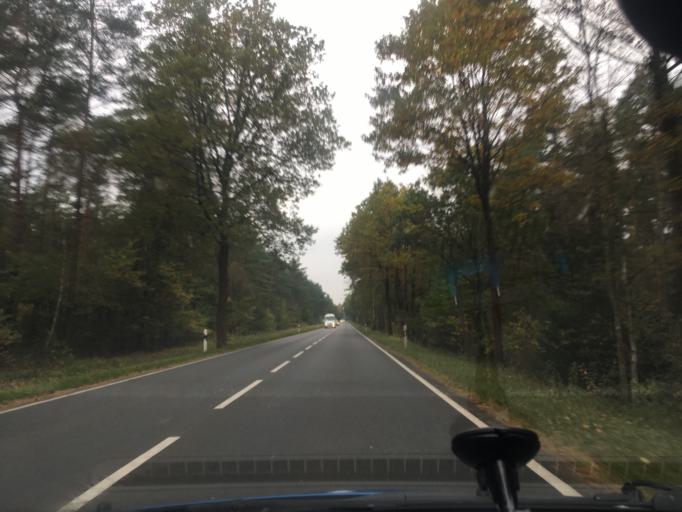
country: DE
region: Lower Saxony
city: Bispingen
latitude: 53.0448
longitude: 9.9934
